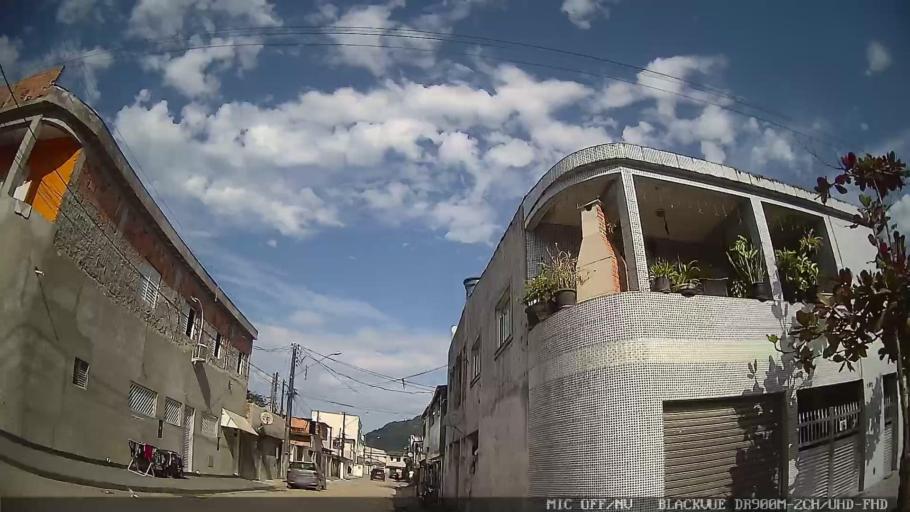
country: BR
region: Sao Paulo
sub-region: Guaruja
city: Guaruja
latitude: -23.9639
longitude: -46.2595
